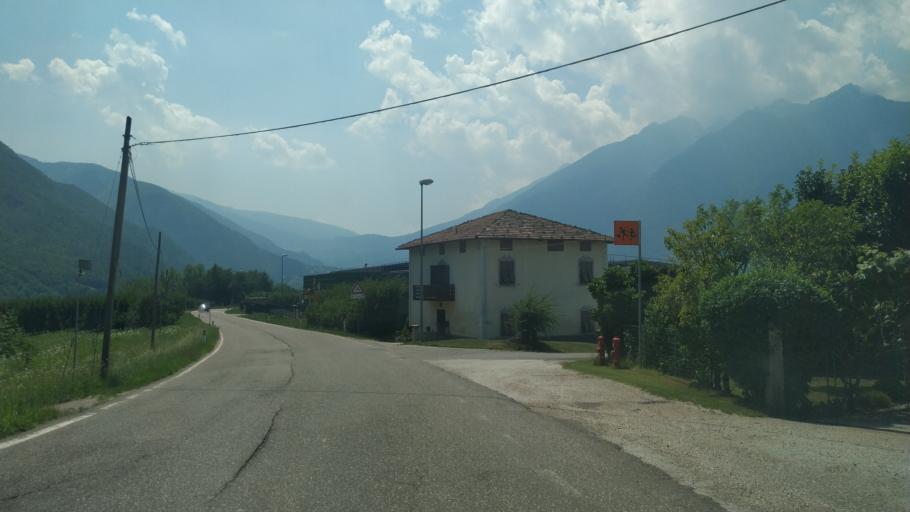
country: IT
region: Trentino-Alto Adige
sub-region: Provincia di Trento
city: Vigo di Ton
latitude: 46.2611
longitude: 11.0748
